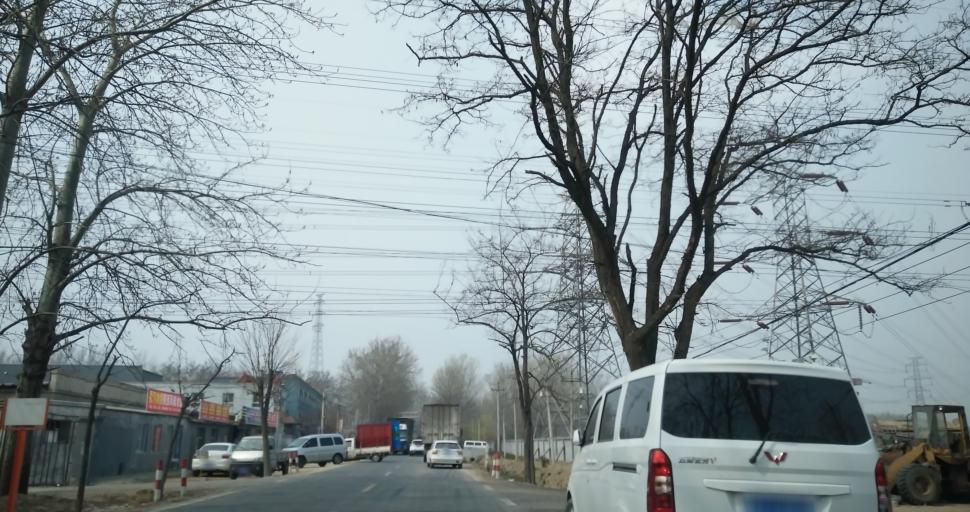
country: CN
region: Beijing
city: Qingyundian
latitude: 39.6898
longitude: 116.4921
